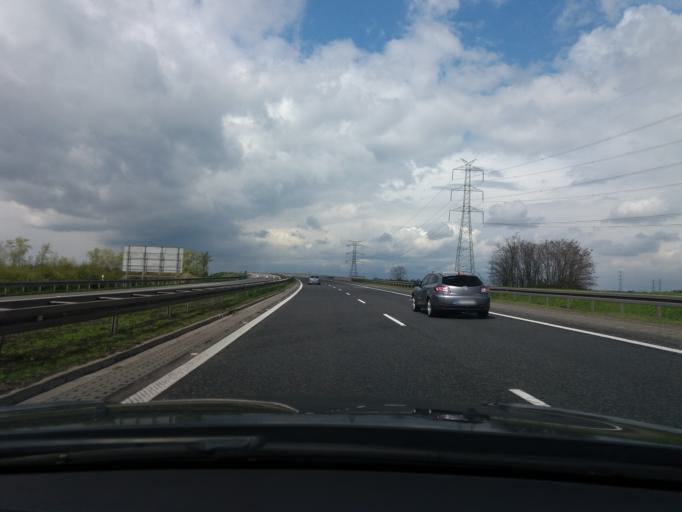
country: PL
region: Lower Silesian Voivodeship
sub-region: Powiat wroclawski
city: Zorawina
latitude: 50.9869
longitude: 17.0571
